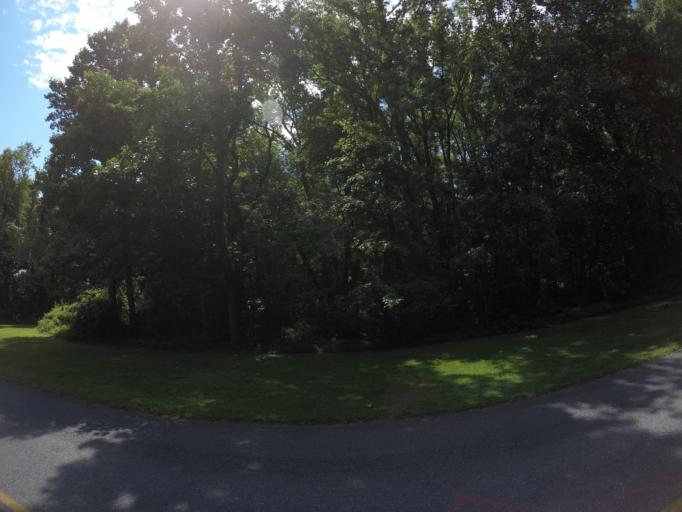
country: US
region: Delaware
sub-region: New Castle County
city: Glasgow
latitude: 39.5631
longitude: -75.7226
